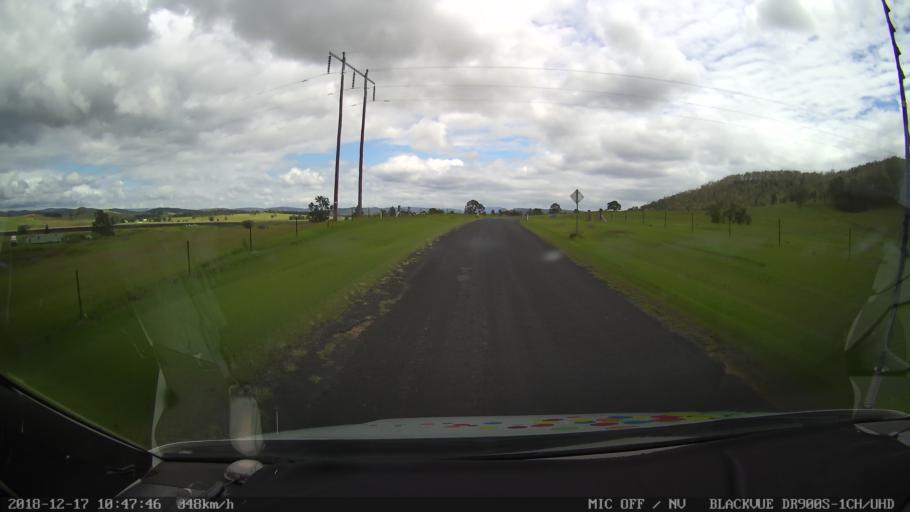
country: AU
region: New South Wales
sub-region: Clarence Valley
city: Gordon
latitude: -28.8784
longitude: 152.5708
